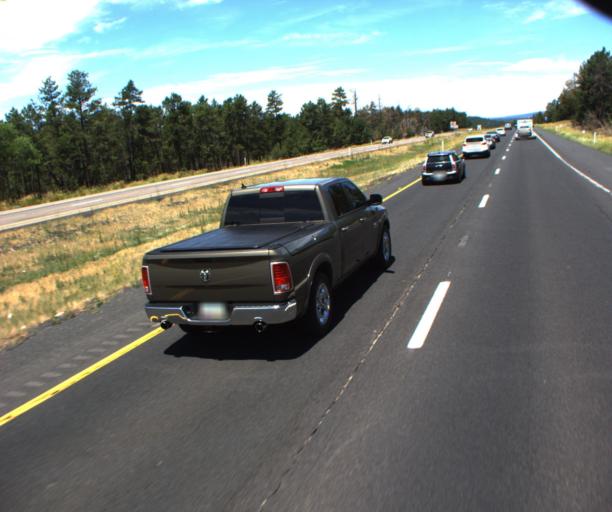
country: US
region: Arizona
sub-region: Coconino County
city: Sedona
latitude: 34.8586
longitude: -111.6119
